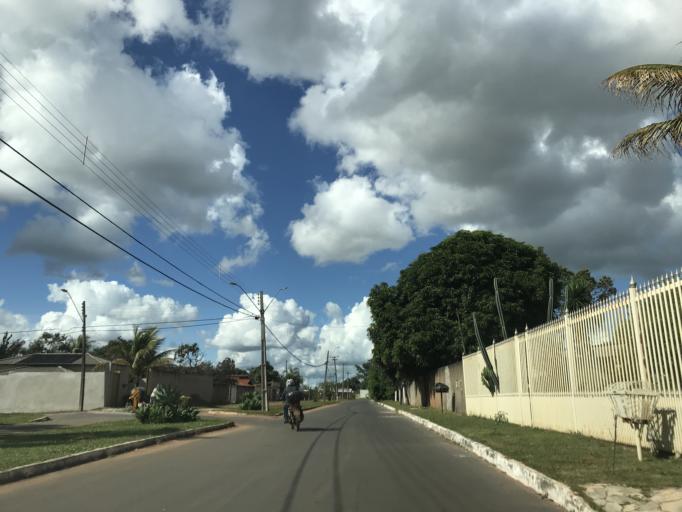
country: BR
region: Federal District
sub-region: Brasilia
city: Brasilia
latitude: -15.7395
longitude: -47.7499
